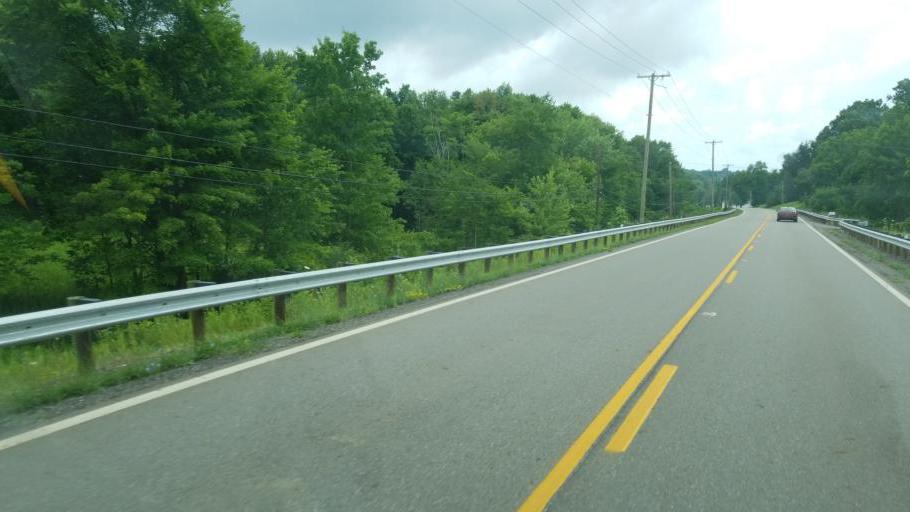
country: US
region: Ohio
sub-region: Columbiana County
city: Lisbon
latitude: 40.7535
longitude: -80.7871
